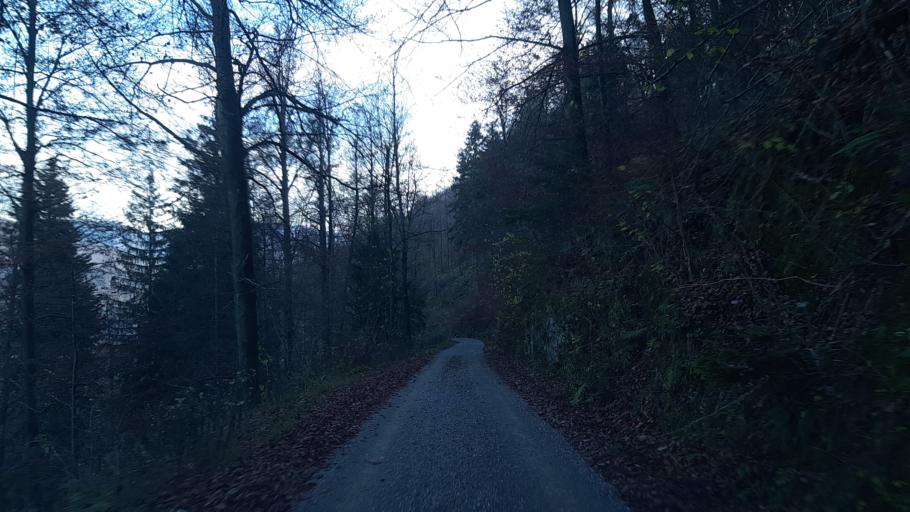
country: SI
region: Borovnica
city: Borovnica
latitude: 45.9286
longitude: 14.3394
